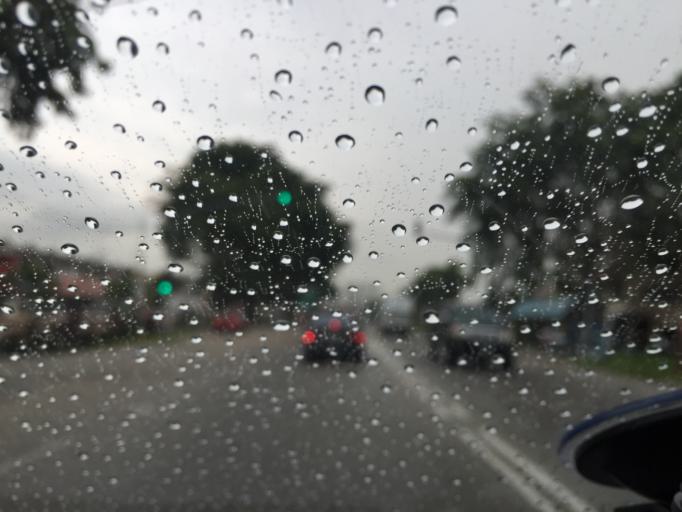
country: MY
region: Selangor
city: Subang Jaya
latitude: 3.0160
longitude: 101.5283
